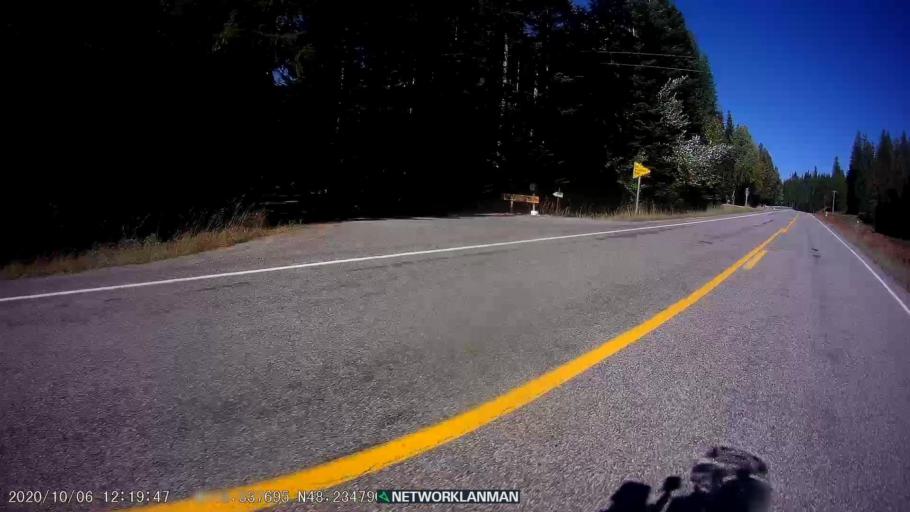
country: US
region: Montana
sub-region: Lincoln County
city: Libby
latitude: 48.2365
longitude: -115.8369
